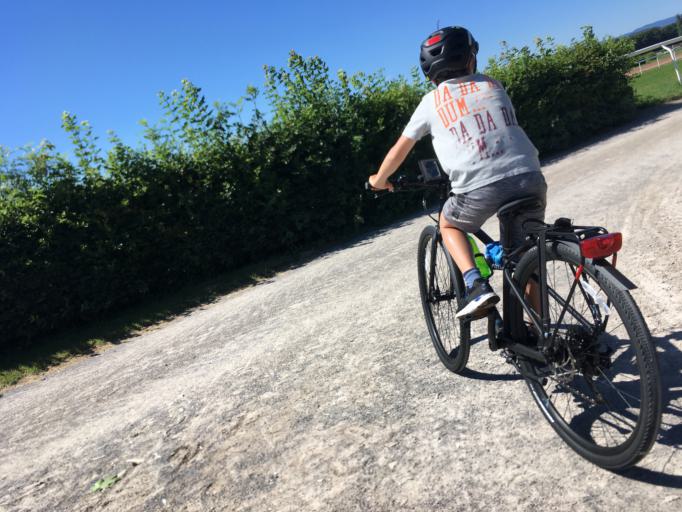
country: CH
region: Fribourg
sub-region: Broye District
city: Domdidier
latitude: 46.8826
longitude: 7.0089
